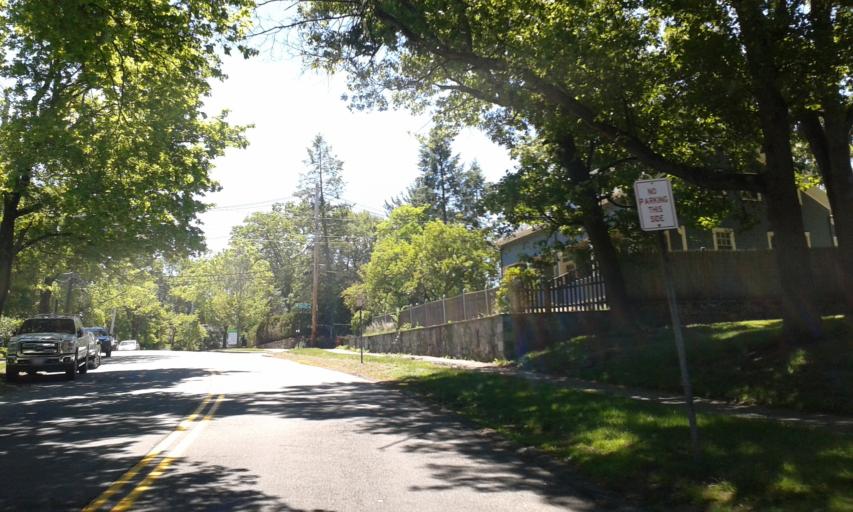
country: US
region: Massachusetts
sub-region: Middlesex County
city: Winchester
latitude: 42.4672
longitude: -71.1211
